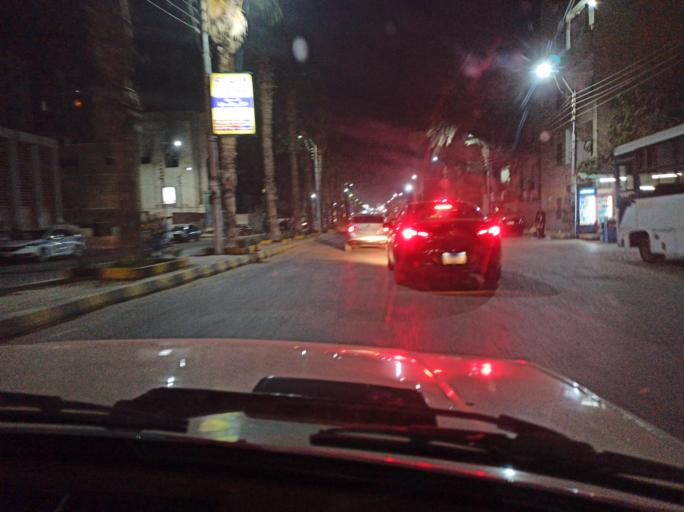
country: EG
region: Muhafazat Bani Suwayf
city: Bani Suwayf
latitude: 29.0739
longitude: 31.1147
